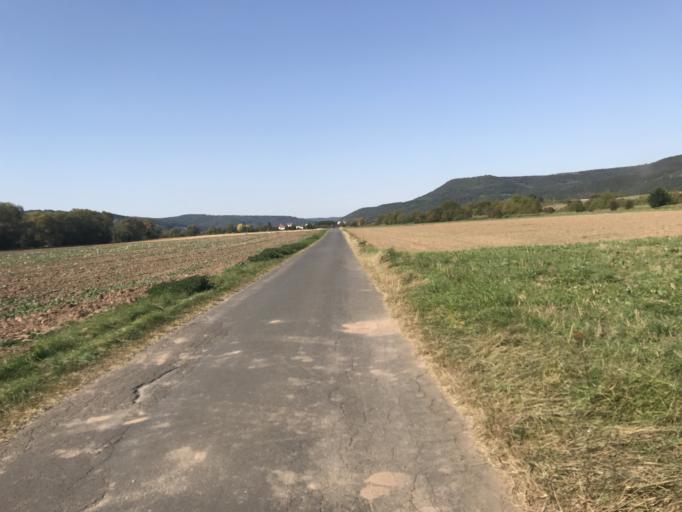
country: DE
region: Thuringia
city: Treffurt
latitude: 51.1275
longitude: 10.1898
